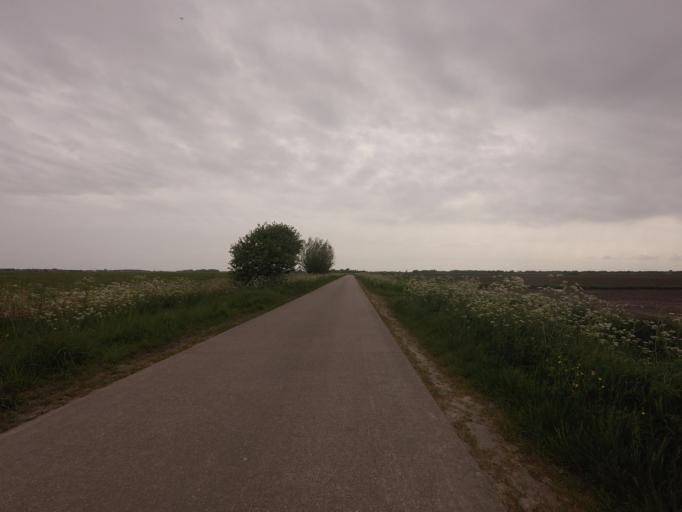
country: NL
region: Zeeland
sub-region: Gemeente Middelburg
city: Middelburg
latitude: 51.5227
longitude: 3.5750
